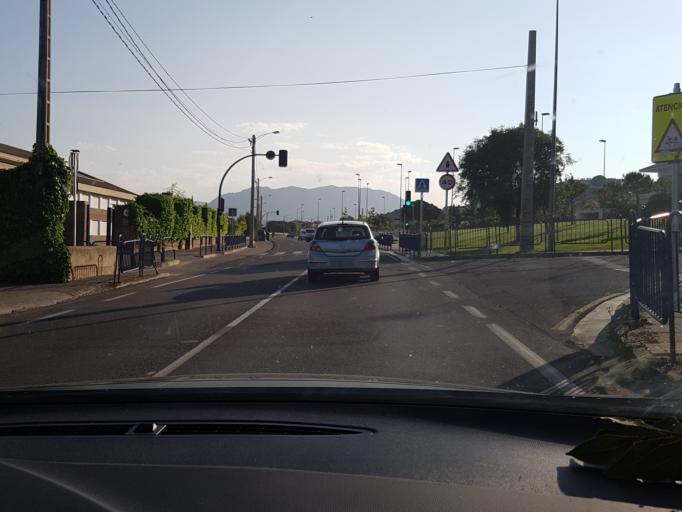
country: ES
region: La Rioja
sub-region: Provincia de La Rioja
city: Arnedo
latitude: 42.2217
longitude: -2.1095
